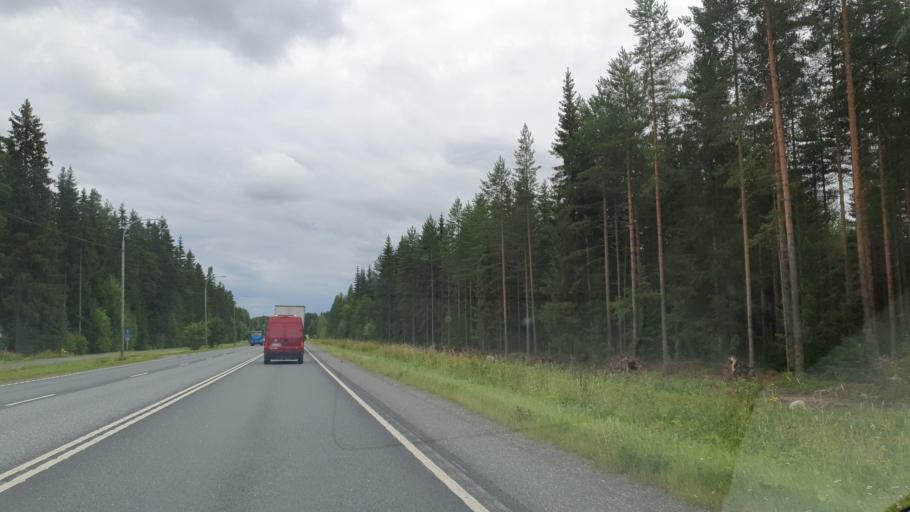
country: FI
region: Northern Savo
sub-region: Ylae-Savo
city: Iisalmi
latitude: 63.4750
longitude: 27.2994
